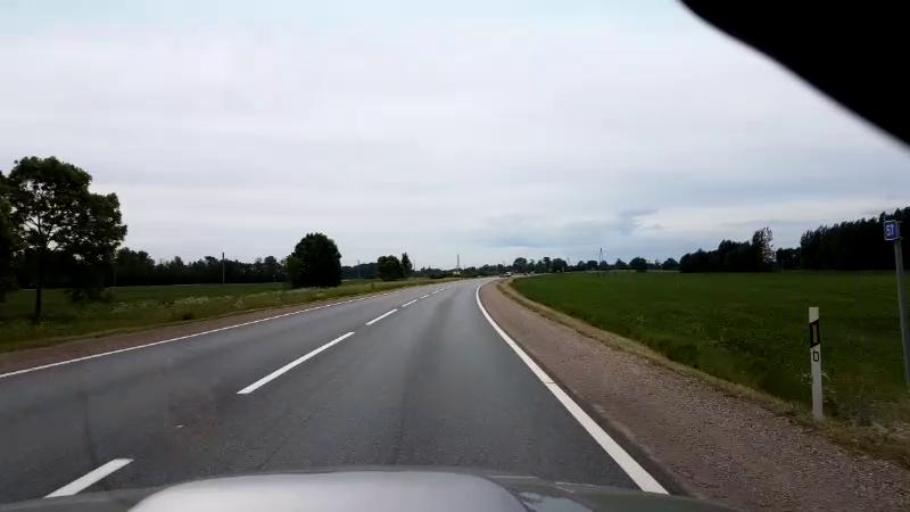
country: LV
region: Bauskas Rajons
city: Bauska
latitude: 56.4818
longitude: 24.1760
